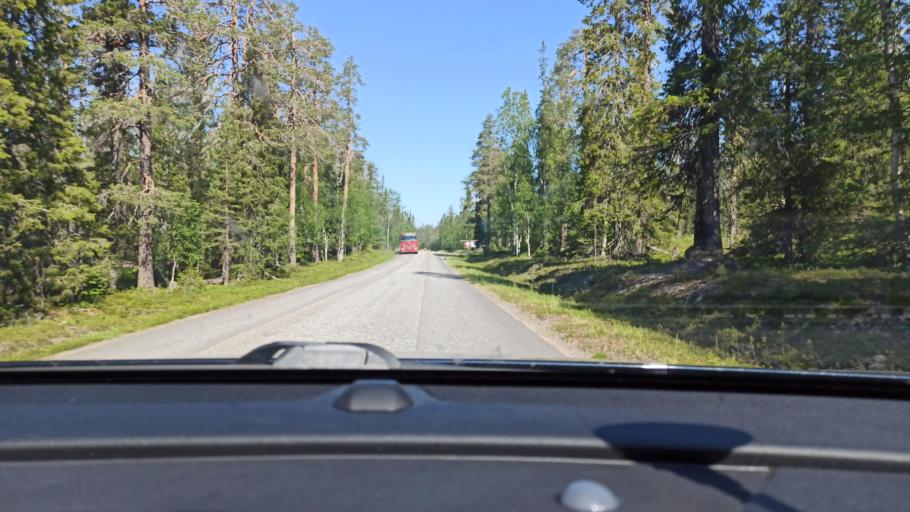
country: FI
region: Lapland
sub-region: Tunturi-Lappi
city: Kolari
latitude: 67.6645
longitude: 24.1621
